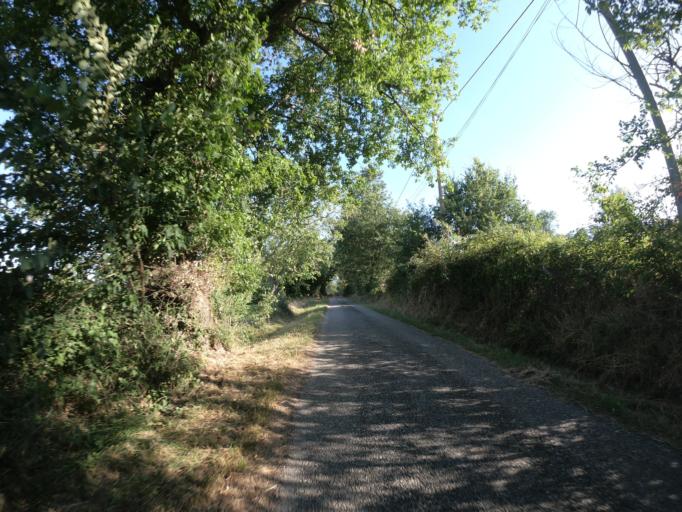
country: FR
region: Midi-Pyrenees
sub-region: Departement de l'Ariege
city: La Tour-du-Crieu
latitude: 43.1086
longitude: 1.7200
